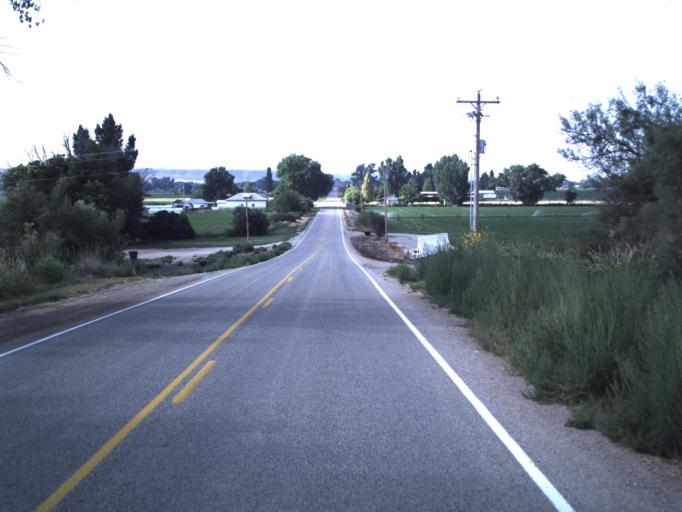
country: US
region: Utah
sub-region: Uintah County
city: Naples
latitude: 40.3878
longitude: -109.3460
